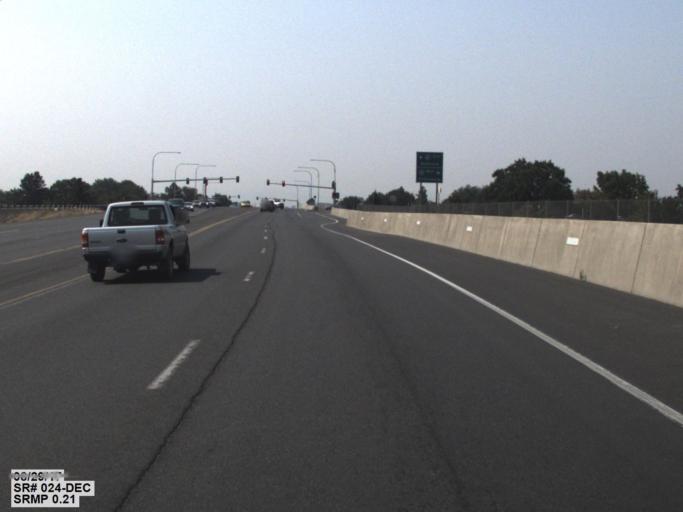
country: US
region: Washington
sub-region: Yakima County
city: Union Gap
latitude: 46.5850
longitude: -120.4688
